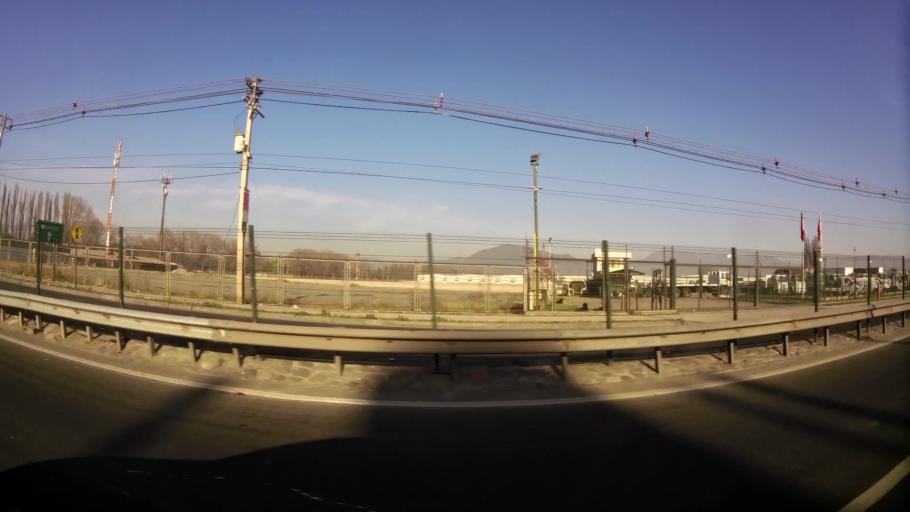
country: CL
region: Santiago Metropolitan
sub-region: Provincia de Santiago
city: Lo Prado
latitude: -33.4620
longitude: -70.7640
